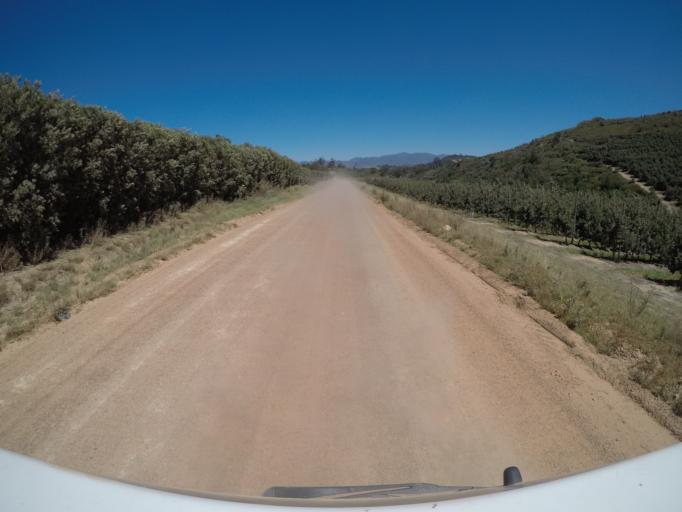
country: ZA
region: Western Cape
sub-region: Overberg District Municipality
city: Grabouw
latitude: -34.2449
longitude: 19.1046
